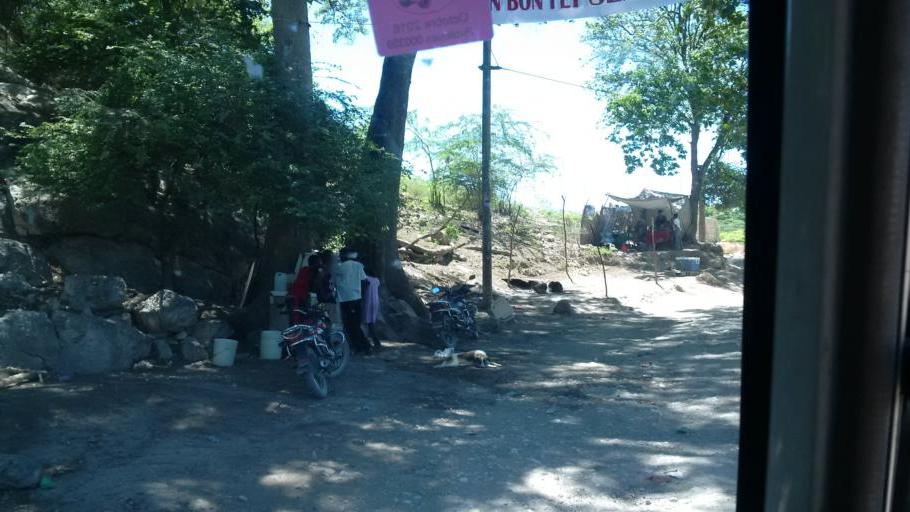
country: HT
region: Ouest
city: Thomazeau
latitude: 18.6572
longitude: -72.1334
